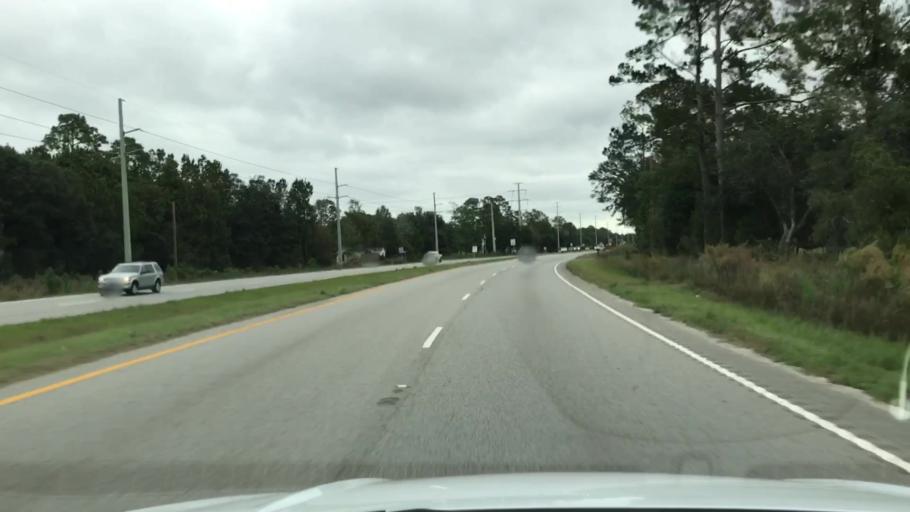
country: US
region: South Carolina
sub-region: Georgetown County
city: Georgetown
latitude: 33.4190
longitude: -79.1790
